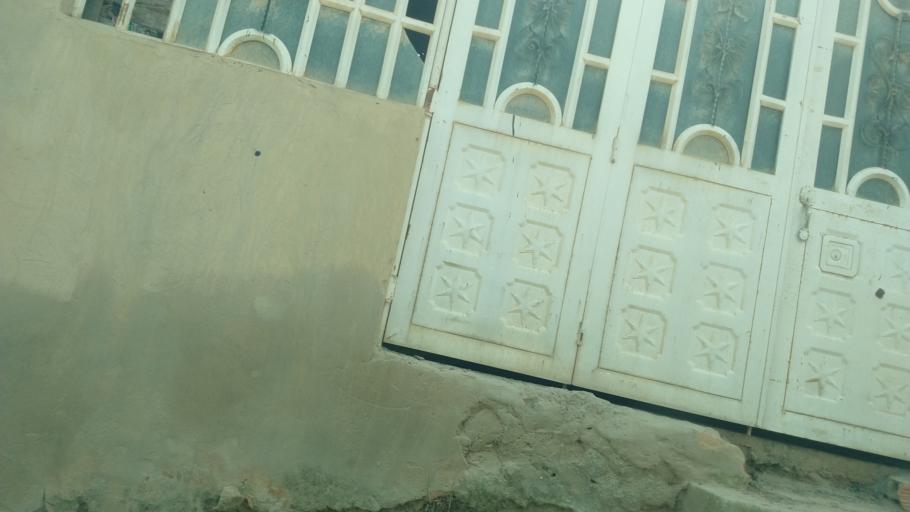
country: CO
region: Cundinamarca
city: Soacha
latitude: 4.5672
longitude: -74.1817
